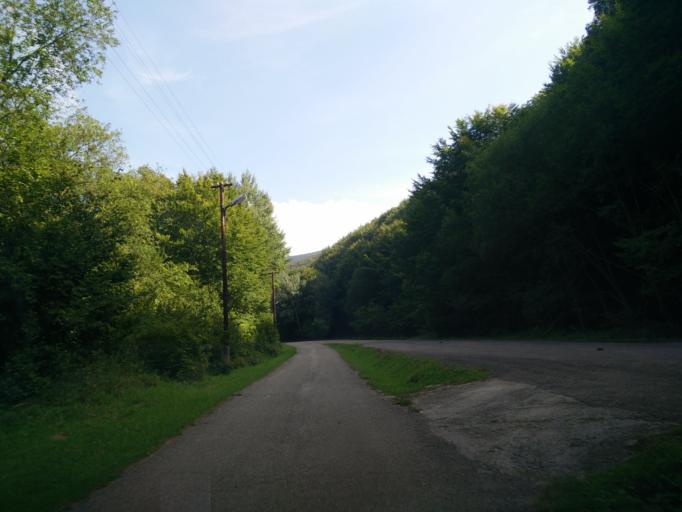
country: SK
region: Nitriansky
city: Novaky
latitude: 48.6628
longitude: 18.6301
